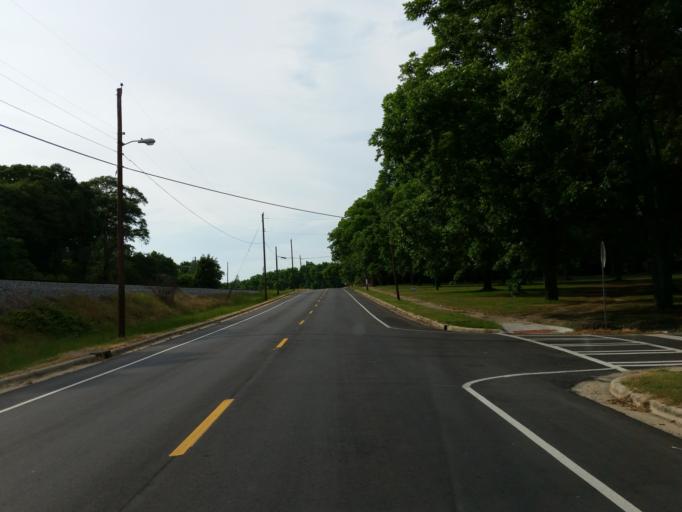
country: US
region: Georgia
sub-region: Turner County
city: Ashburn
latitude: 31.7141
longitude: -83.6576
